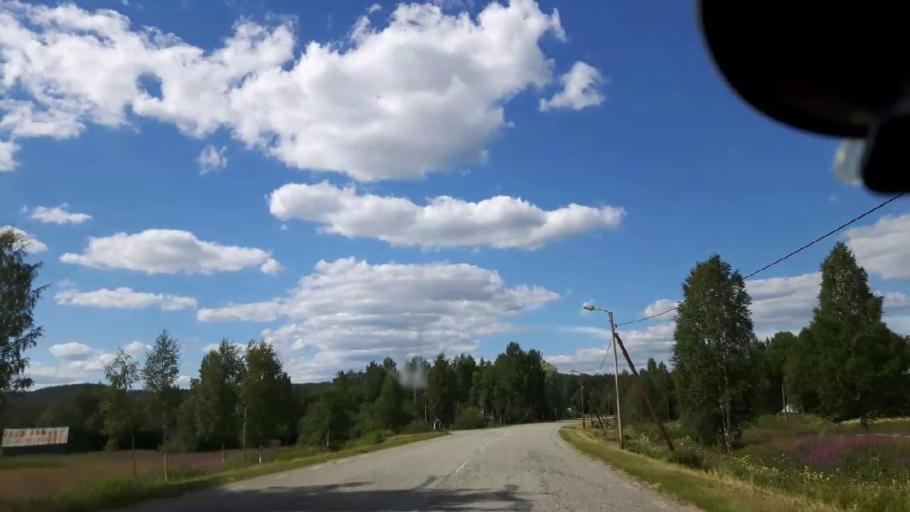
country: SE
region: Vaesternorrland
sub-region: Ange Kommun
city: Fransta
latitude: 62.7939
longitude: 16.2127
